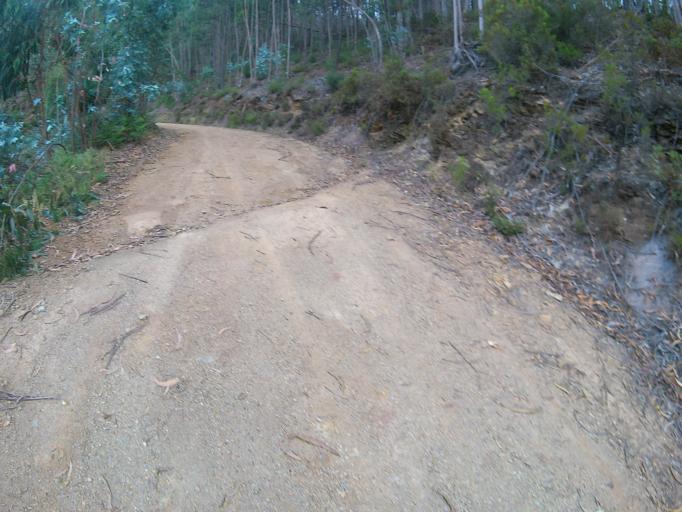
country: PT
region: Aveiro
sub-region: Albergaria-A-Velha
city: Branca
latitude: 40.7582
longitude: -8.4289
